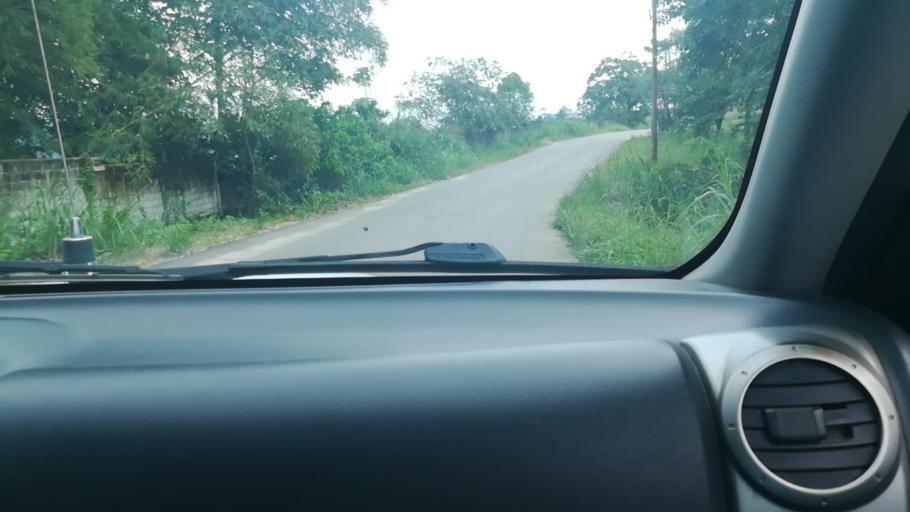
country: EC
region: Napo
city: Tena
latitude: -0.9746
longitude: -77.8149
